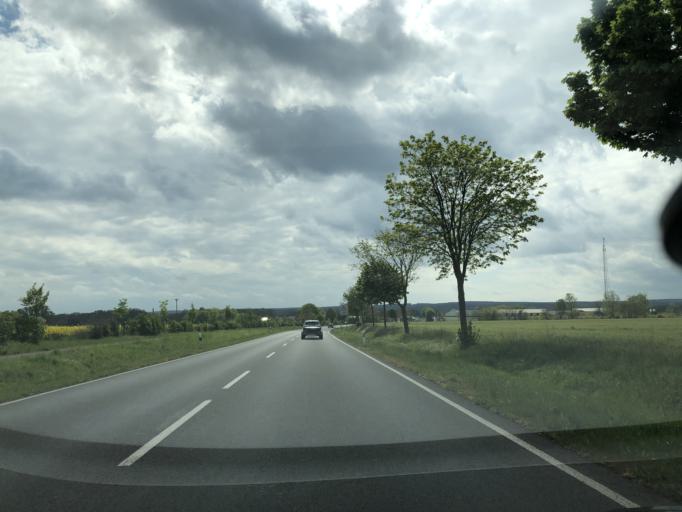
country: DE
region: Saxony-Anhalt
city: Luderitz
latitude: 52.5160
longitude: 11.7515
